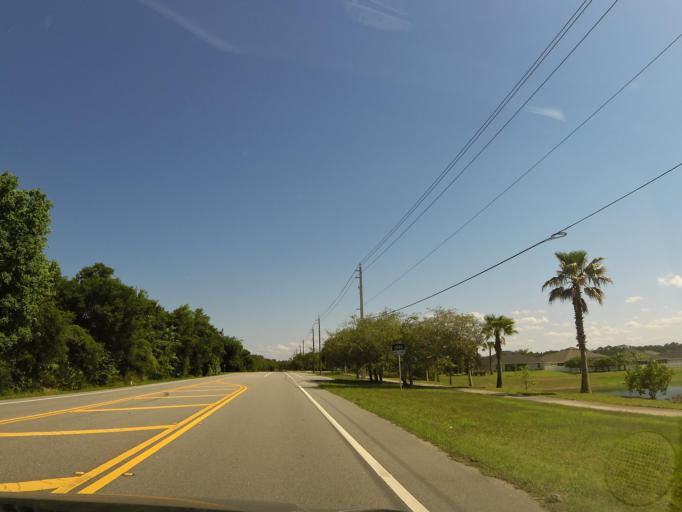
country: US
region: Florida
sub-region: Flagler County
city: Flagler Beach
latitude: 29.4214
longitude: -81.1502
